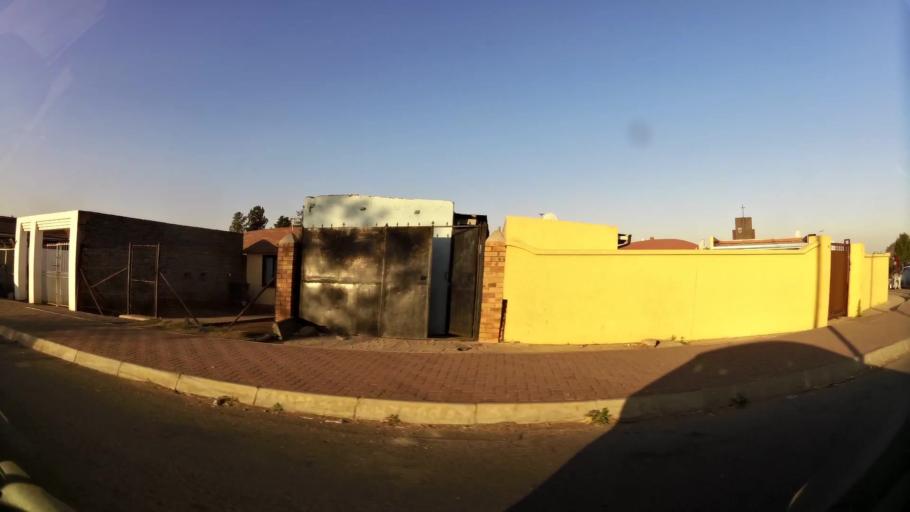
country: ZA
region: Gauteng
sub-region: City of Johannesburg Metropolitan Municipality
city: Soweto
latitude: -26.2478
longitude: 27.8777
